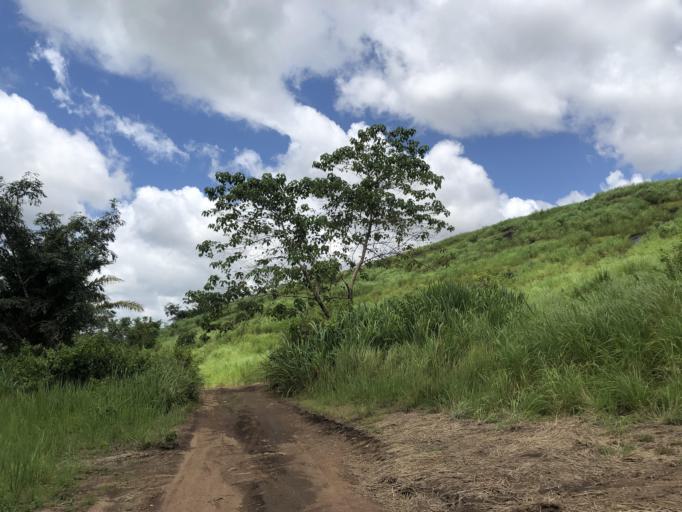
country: SL
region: Northern Province
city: Makeni
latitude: 8.8535
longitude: -12.0624
